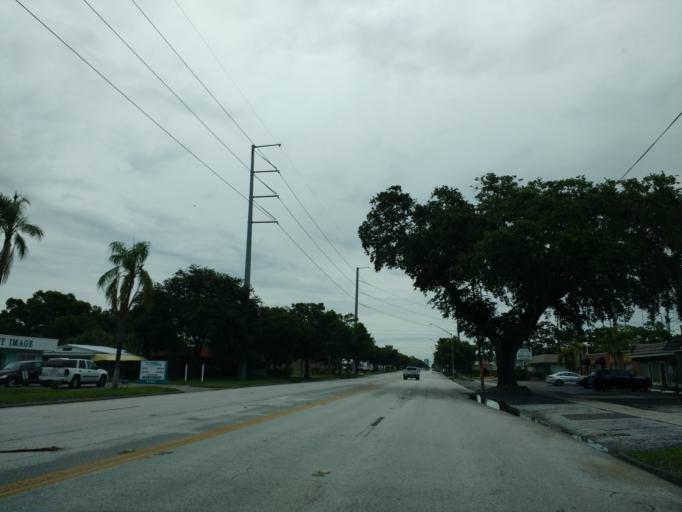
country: US
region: Florida
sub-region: Pinellas County
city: Gulfport
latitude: 27.7709
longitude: -82.7037
